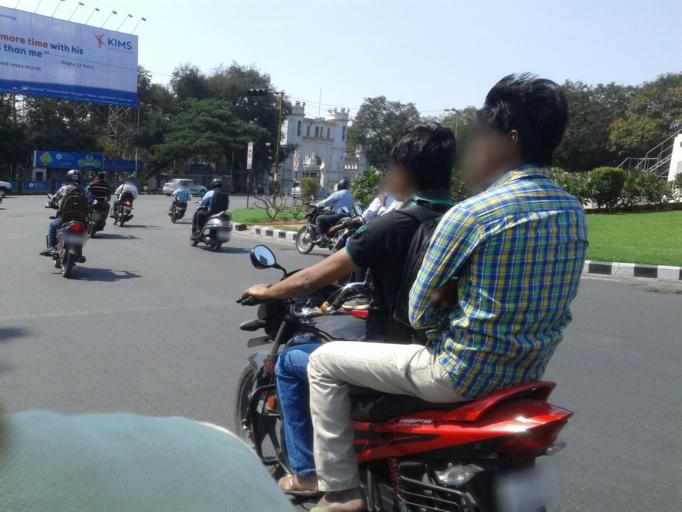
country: IN
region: Telangana
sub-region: Hyderabad
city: Hyderabad
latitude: 17.4006
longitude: 78.4705
